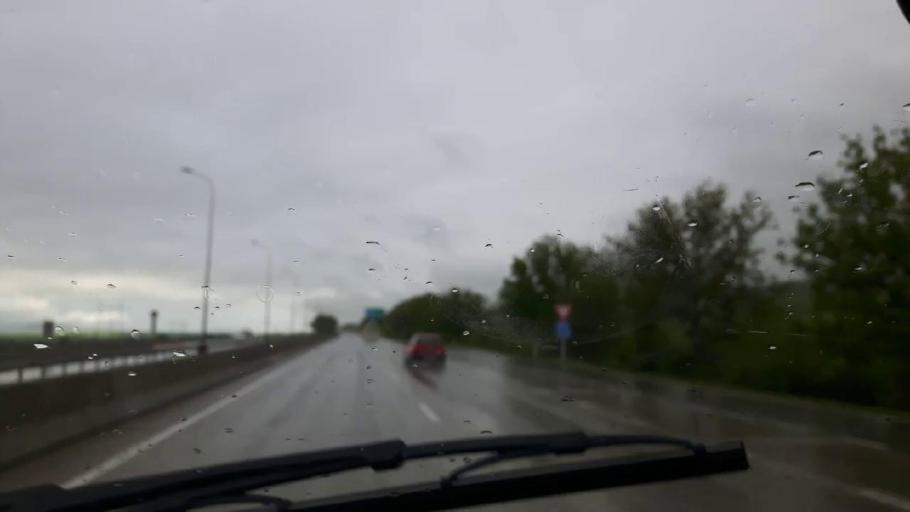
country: GE
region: Shida Kartli
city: Kaspi
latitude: 42.0146
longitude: 44.3241
